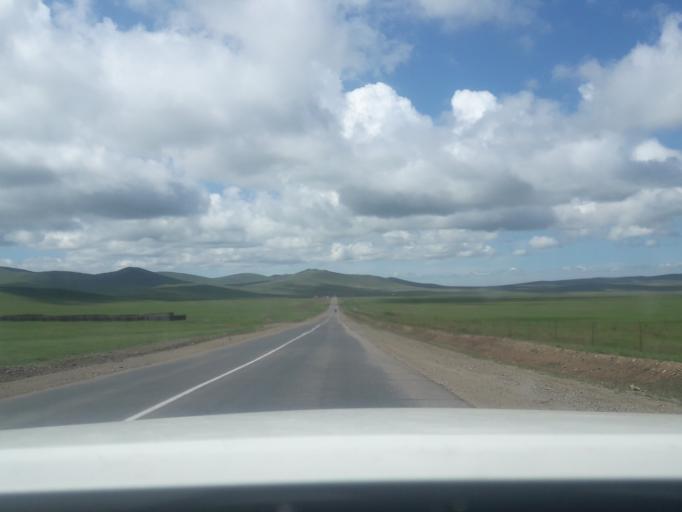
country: MN
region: Central Aimak
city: Altanbulag
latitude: 47.9007
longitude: 106.4688
